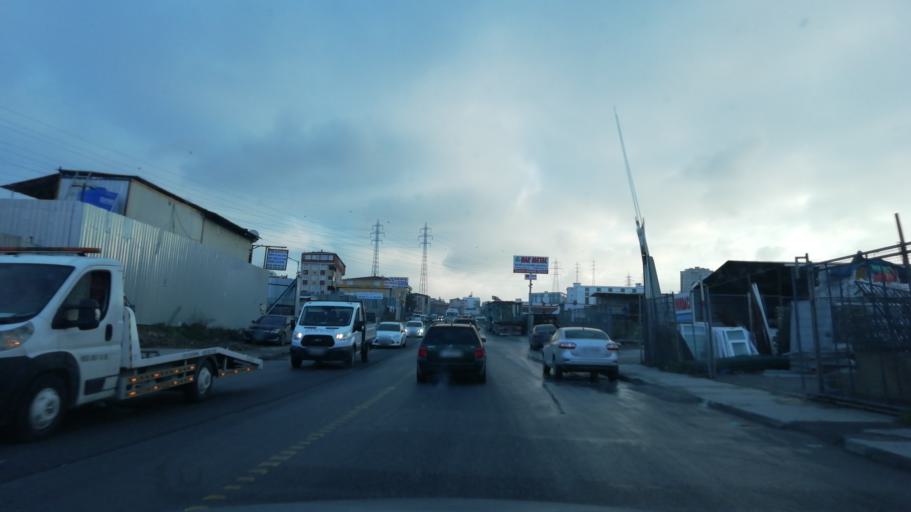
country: TR
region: Istanbul
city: Esenyurt
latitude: 41.0245
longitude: 28.7015
